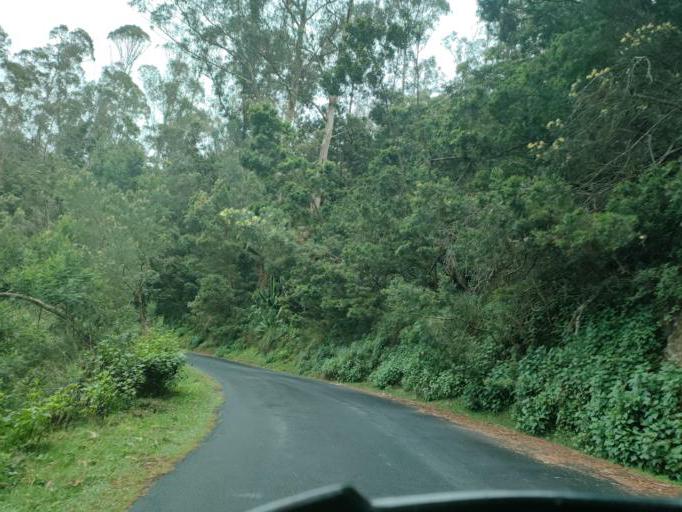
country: IN
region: Tamil Nadu
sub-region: Dindigul
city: Kodaikanal
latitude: 10.2412
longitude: 77.3663
